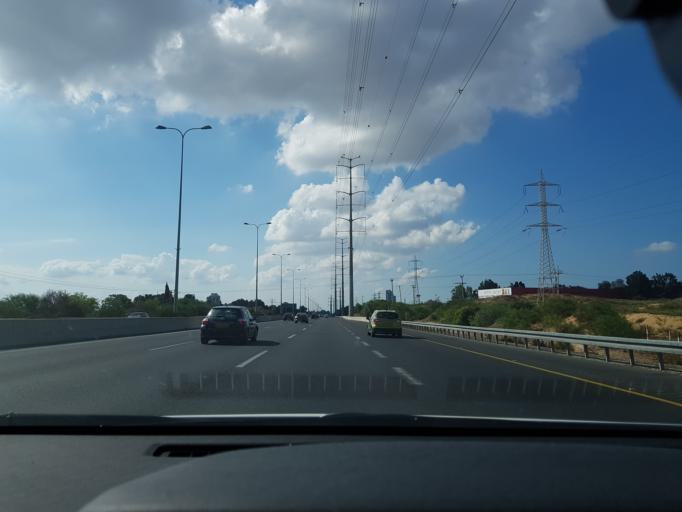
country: IL
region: Central District
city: Rishon LeZiyyon
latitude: 31.9909
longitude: 34.7979
